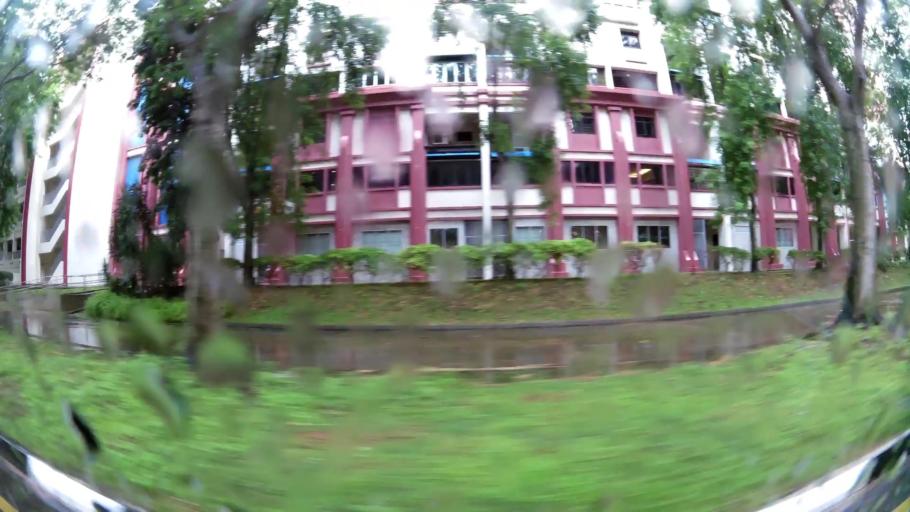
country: MY
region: Johor
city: Kampung Pasir Gudang Baru
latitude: 1.3816
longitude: 103.9005
